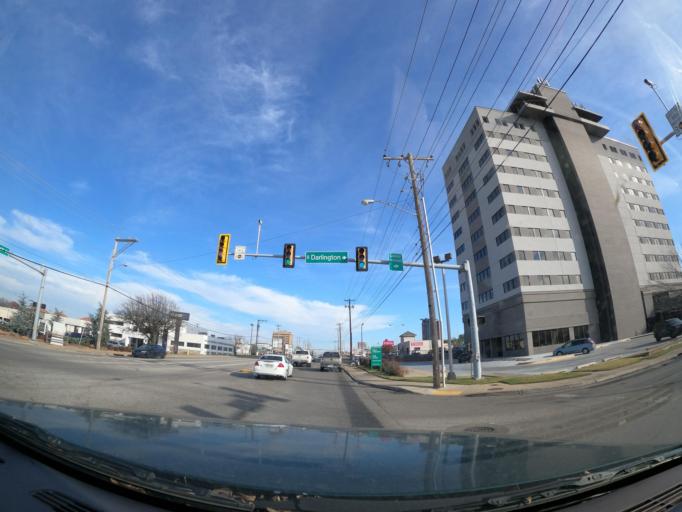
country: US
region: Oklahoma
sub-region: Tulsa County
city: Tulsa
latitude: 36.1044
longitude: -95.9173
